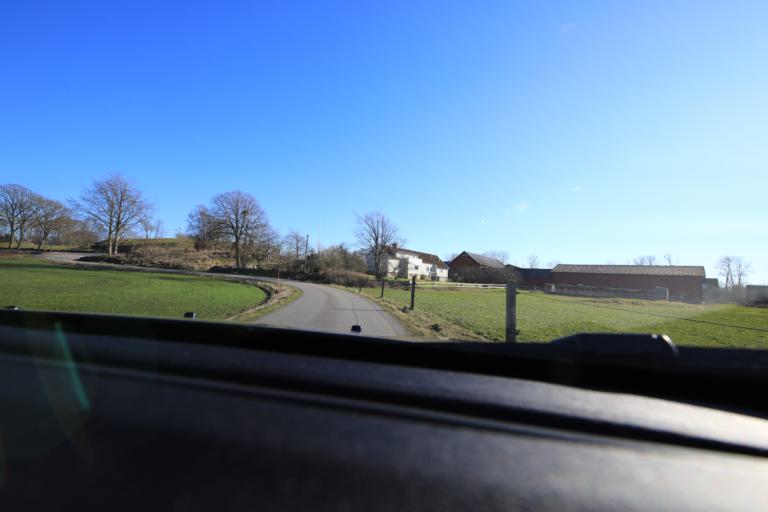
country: SE
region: Halland
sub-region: Varbergs Kommun
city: Tvaaker
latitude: 57.0533
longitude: 12.3750
